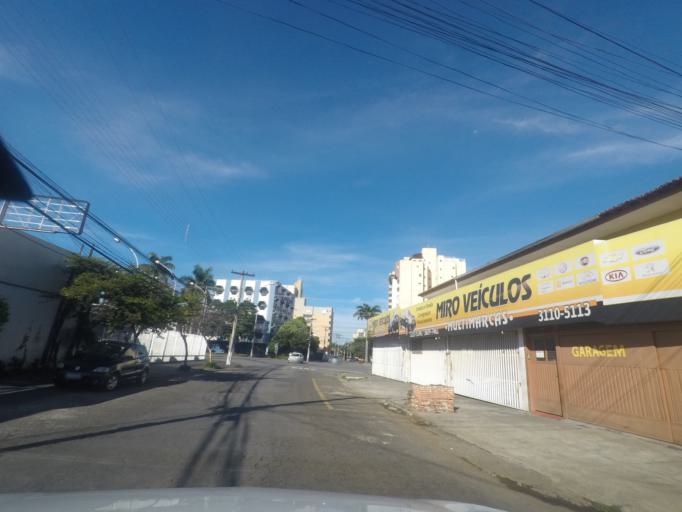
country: BR
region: Goias
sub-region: Goiania
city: Goiania
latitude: -16.6726
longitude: -49.2687
